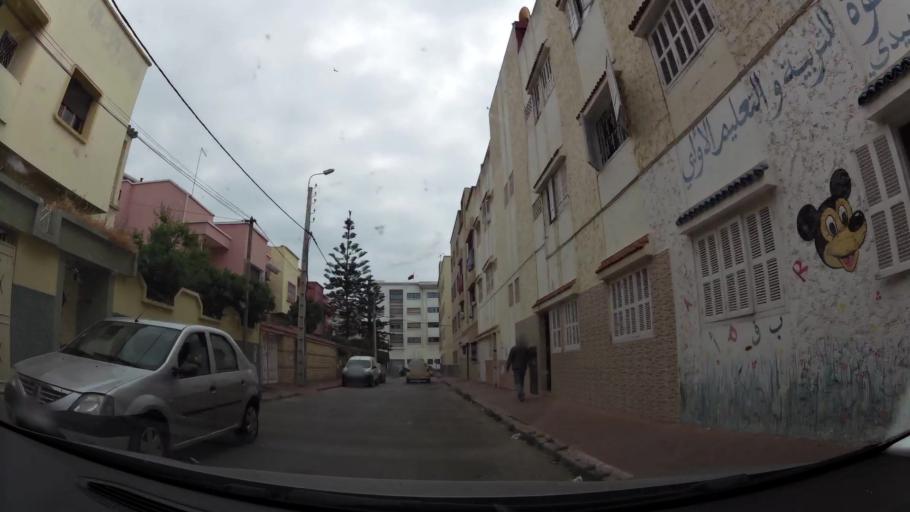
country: MA
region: Rabat-Sale-Zemmour-Zaer
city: Sale
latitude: 34.0295
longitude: -6.7998
